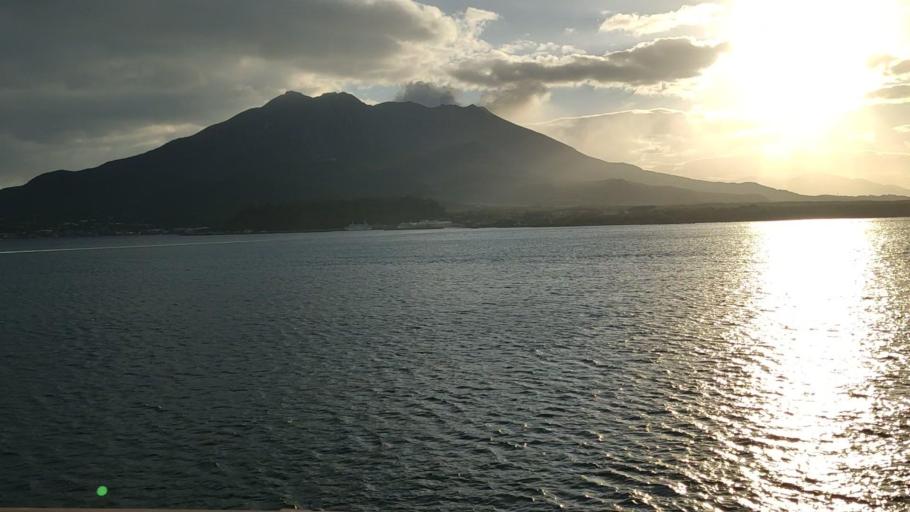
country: JP
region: Kagoshima
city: Kagoshima-shi
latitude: 31.5960
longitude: 130.5793
